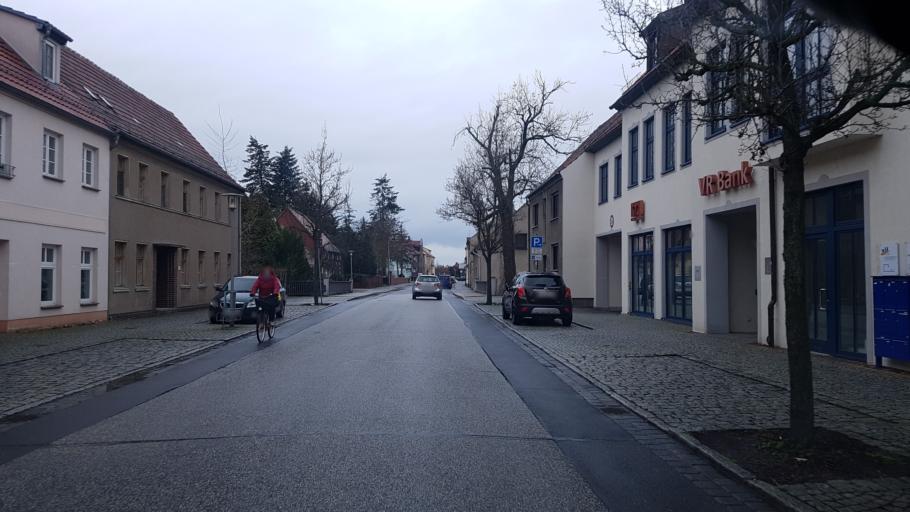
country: DE
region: Brandenburg
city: Herzberg
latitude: 51.6907
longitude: 13.2298
